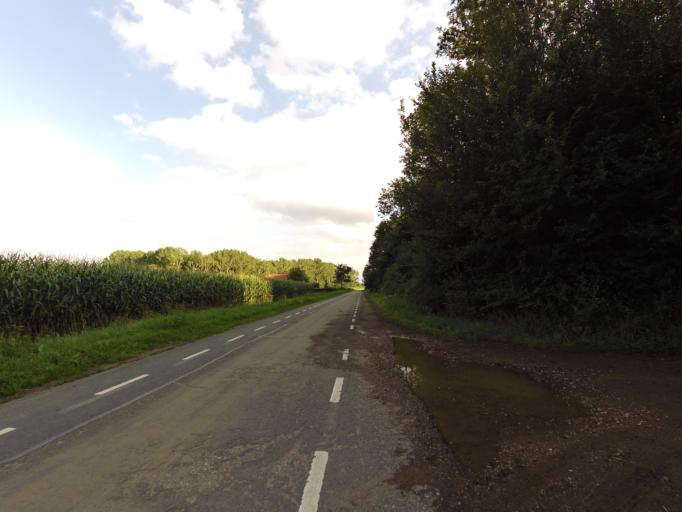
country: NL
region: Gelderland
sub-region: Gemeente Doesburg
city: Doesburg
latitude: 51.9812
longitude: 6.1608
